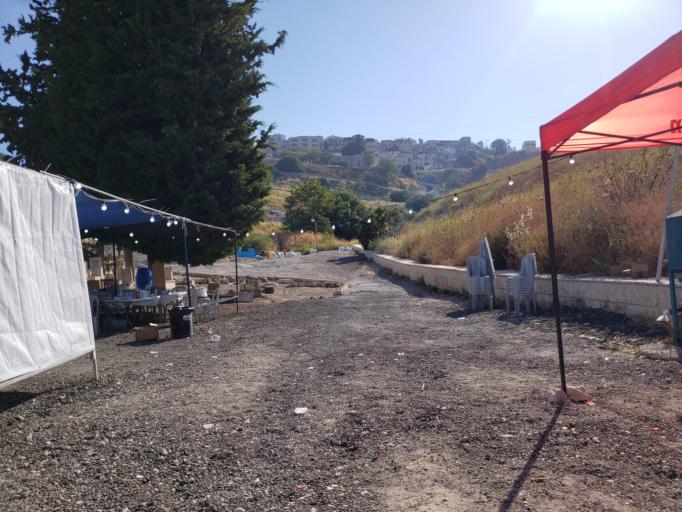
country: IL
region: Northern District
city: Safed
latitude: 32.9671
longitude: 35.4875
